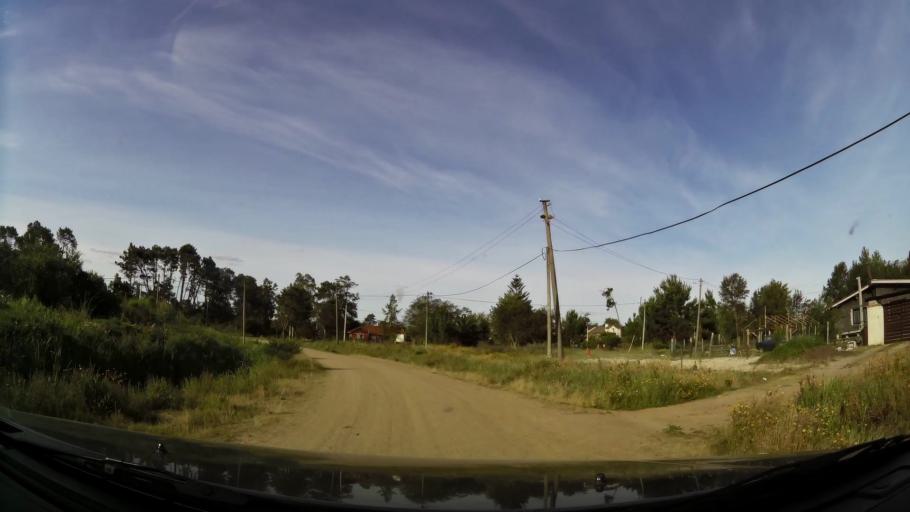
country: UY
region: Canelones
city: Empalme Olmos
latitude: -34.7899
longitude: -55.8574
